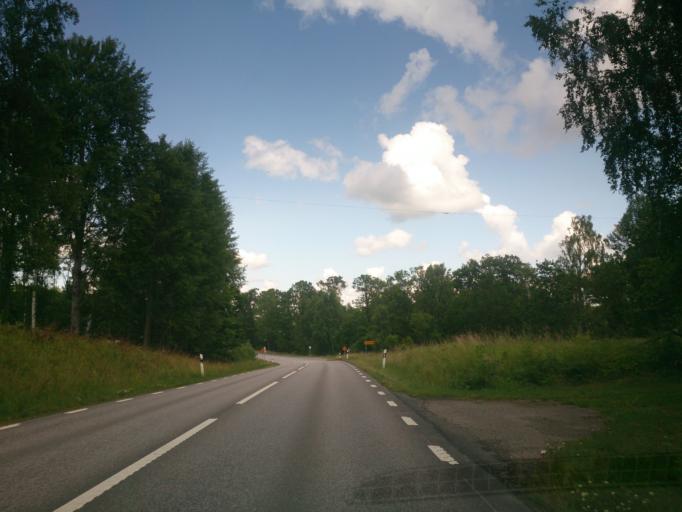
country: SE
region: OEstergoetland
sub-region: Atvidabergs Kommun
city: Atvidaberg
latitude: 58.2520
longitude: 15.9303
